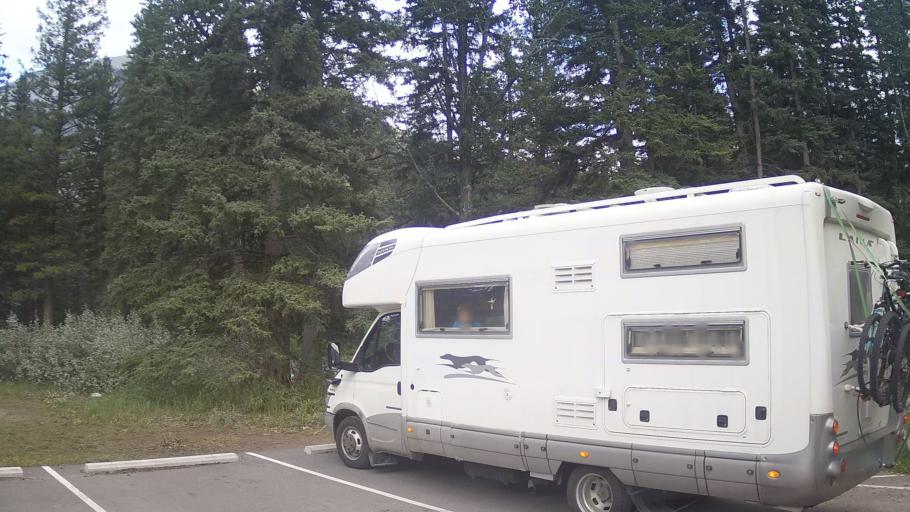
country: CA
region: Alberta
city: Jasper Park Lodge
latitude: 52.9332
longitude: -118.0304
